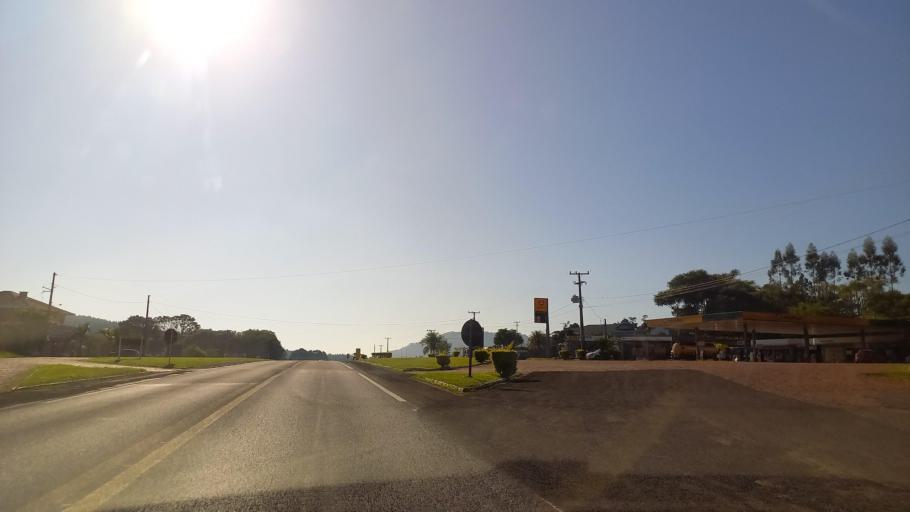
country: BR
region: Rio Grande do Sul
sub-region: Taquari
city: Taquari
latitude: -29.7100
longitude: -51.7665
